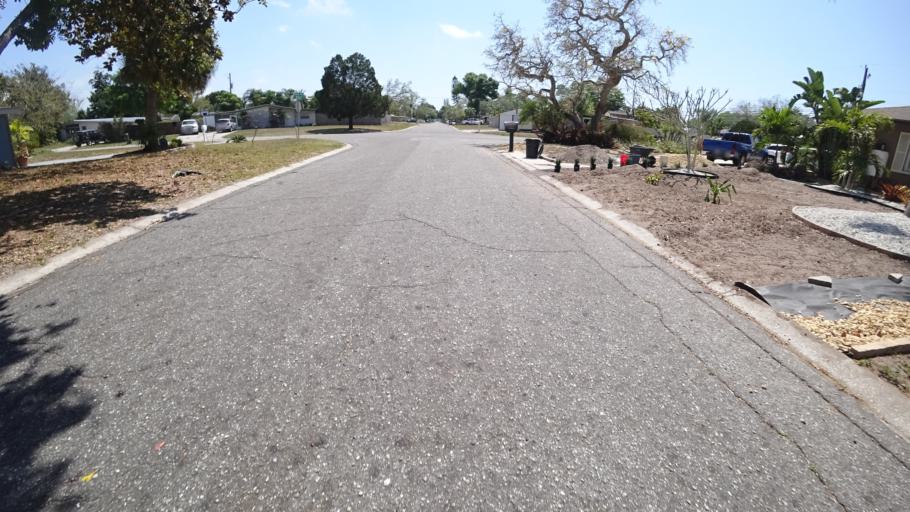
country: US
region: Florida
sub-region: Manatee County
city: Bayshore Gardens
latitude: 27.4292
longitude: -82.5869
